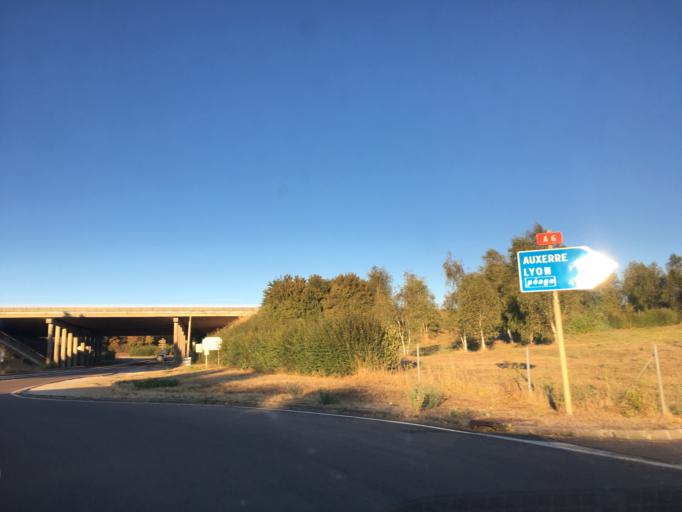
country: FR
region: Bourgogne
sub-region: Departement de l'Yonne
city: Saint-Julien-du-Sault
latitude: 47.9382
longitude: 3.2428
